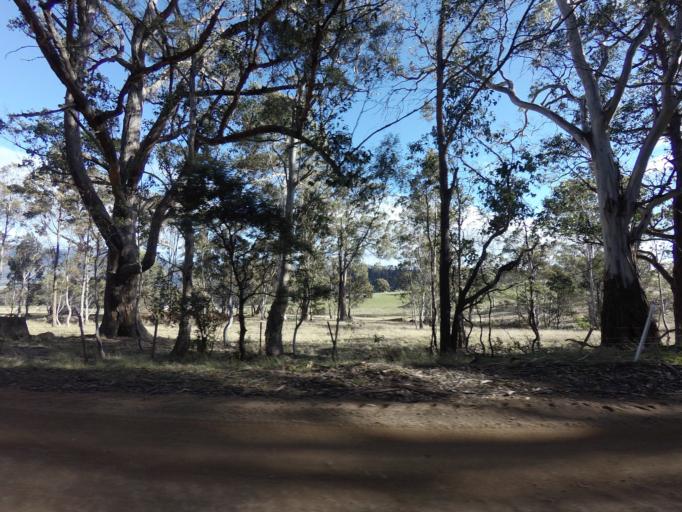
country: AU
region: Tasmania
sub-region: Derwent Valley
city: New Norfolk
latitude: -42.7152
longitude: 147.0317
